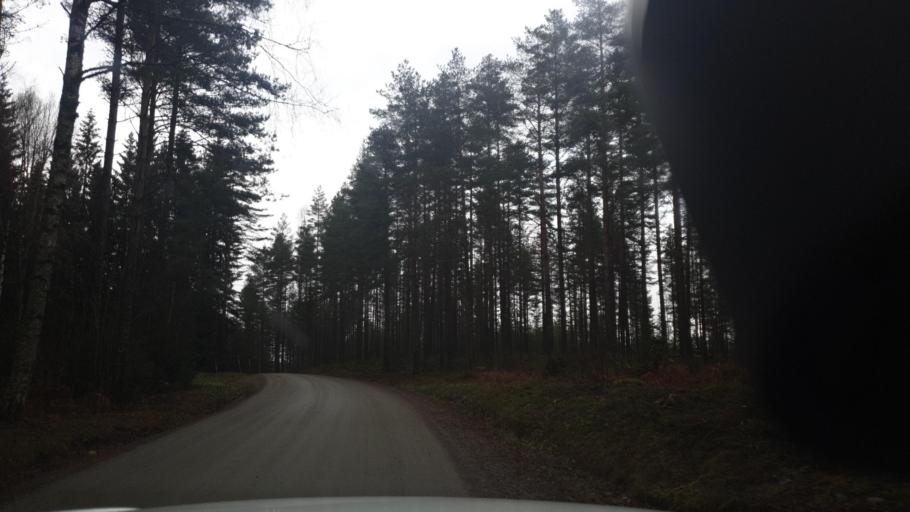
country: SE
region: Vaermland
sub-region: Karlstads Kommun
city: Edsvalla
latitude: 59.5849
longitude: 13.0771
